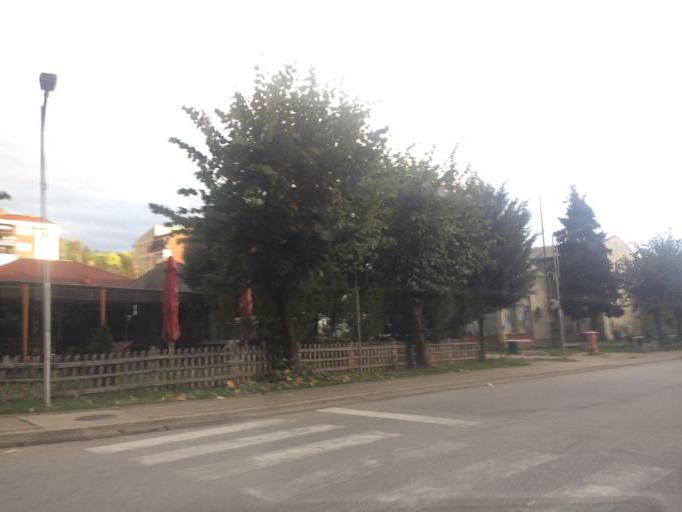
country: MK
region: Makedonska Kamenica
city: Makedonska Kamenica
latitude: 42.0197
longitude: 22.5896
